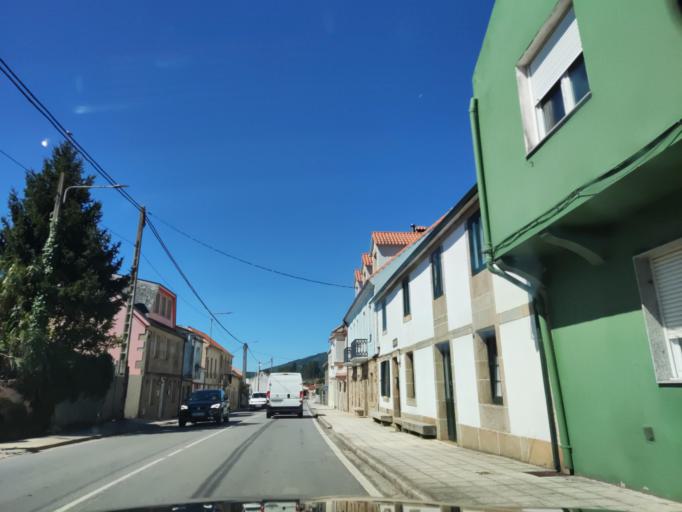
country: ES
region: Galicia
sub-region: Provincia da Coruna
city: Boiro
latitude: 42.6182
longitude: -8.9258
